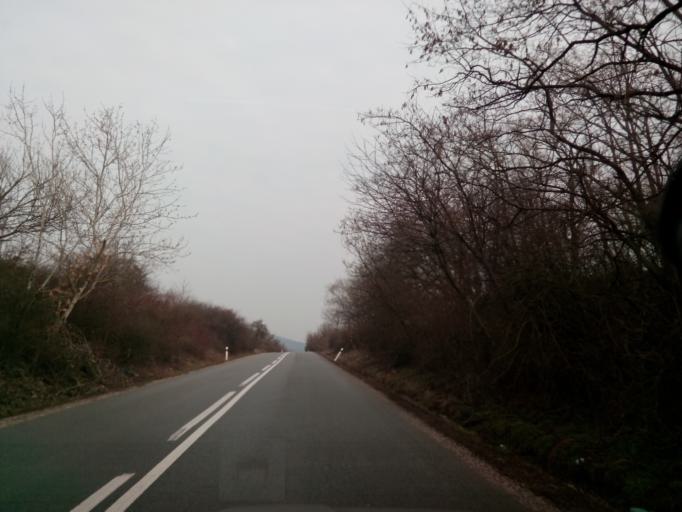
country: SK
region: Kosicky
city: Secovce
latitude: 48.6301
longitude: 21.5543
